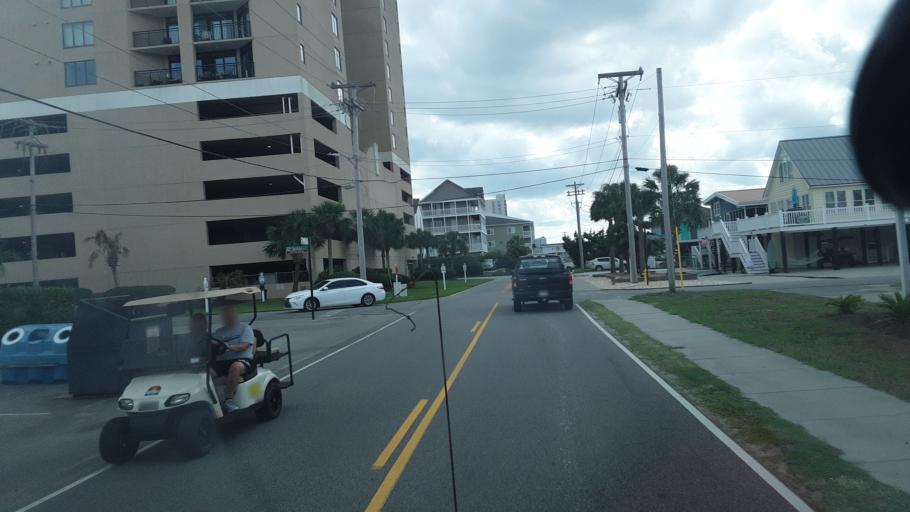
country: US
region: South Carolina
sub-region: Horry County
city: Little River
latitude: 33.8337
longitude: -78.6270
